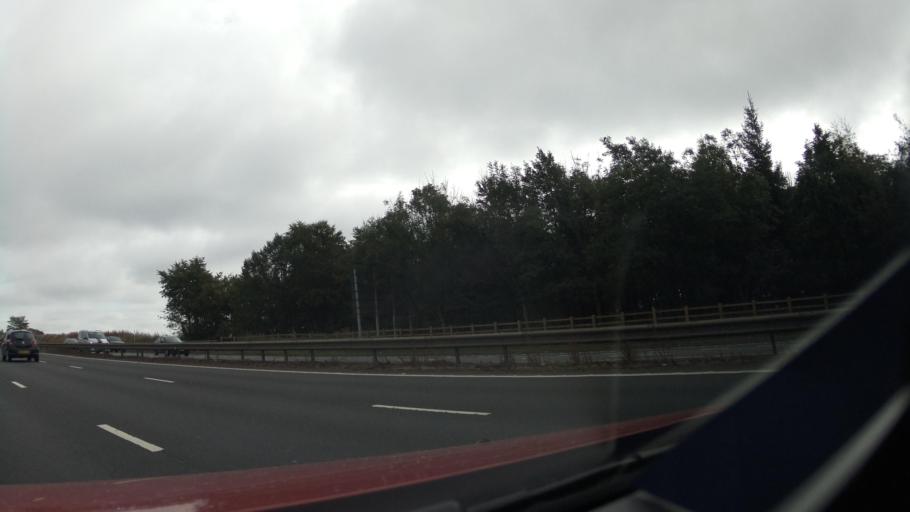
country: GB
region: Scotland
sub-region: Falkirk
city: Dunipace
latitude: 55.9968
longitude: -3.9331
